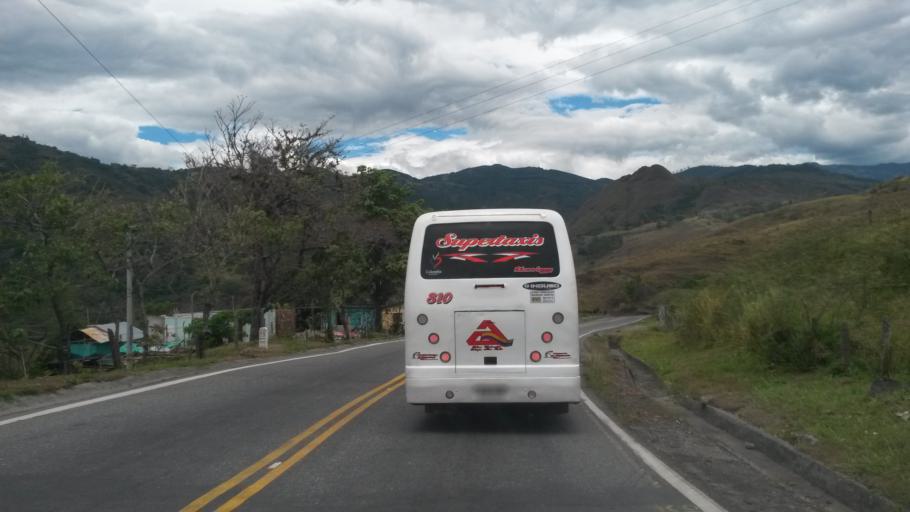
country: CO
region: Cauca
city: Rosas
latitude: 2.2816
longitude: -76.7202
